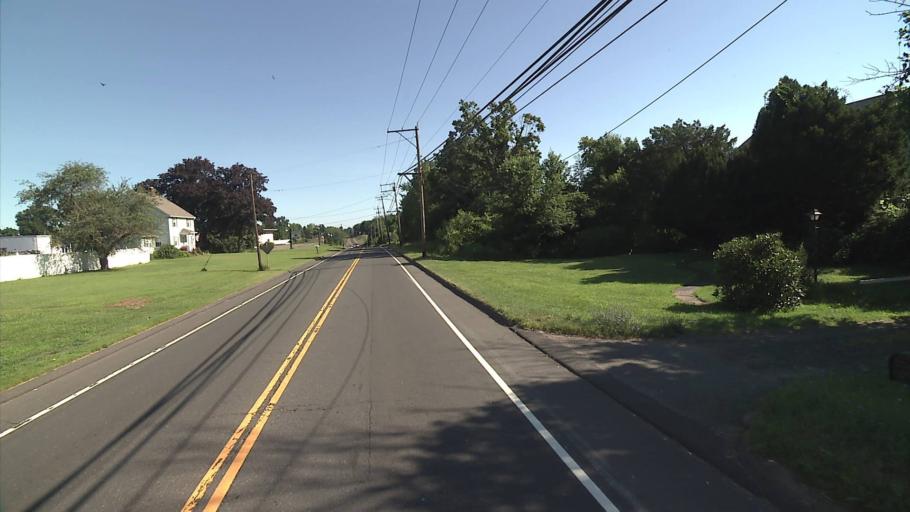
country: US
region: Connecticut
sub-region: New Haven County
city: Cheshire Village
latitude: 41.5446
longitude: -72.8920
